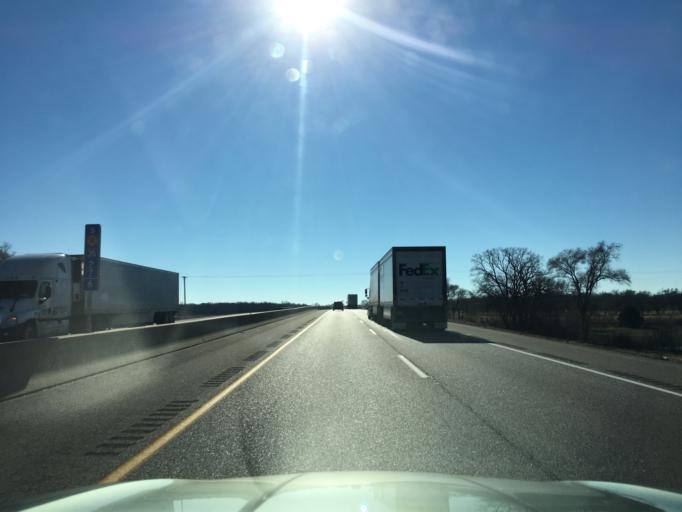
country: US
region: Kansas
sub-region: Sumner County
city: Belle Plaine
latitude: 37.3940
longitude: -97.3259
